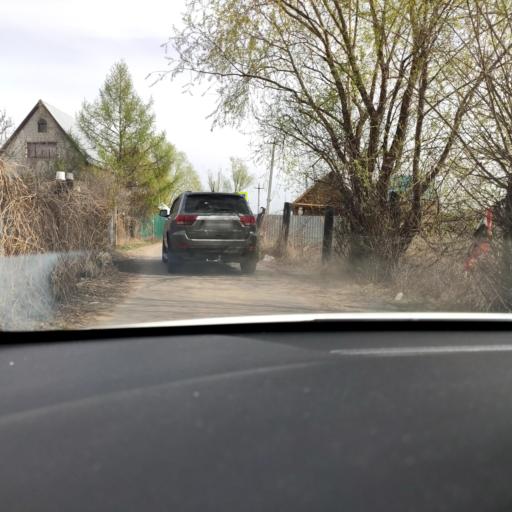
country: RU
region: Tatarstan
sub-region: Gorod Kazan'
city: Kazan
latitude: 55.8503
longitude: 49.1652
